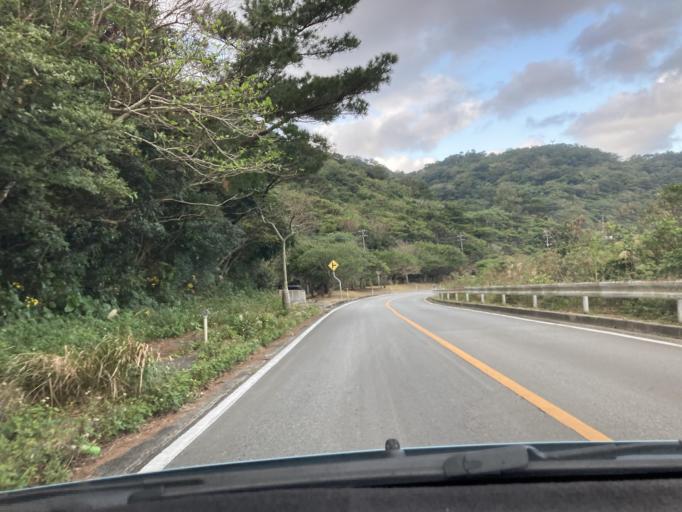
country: JP
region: Okinawa
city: Nago
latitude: 26.8346
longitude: 128.2870
